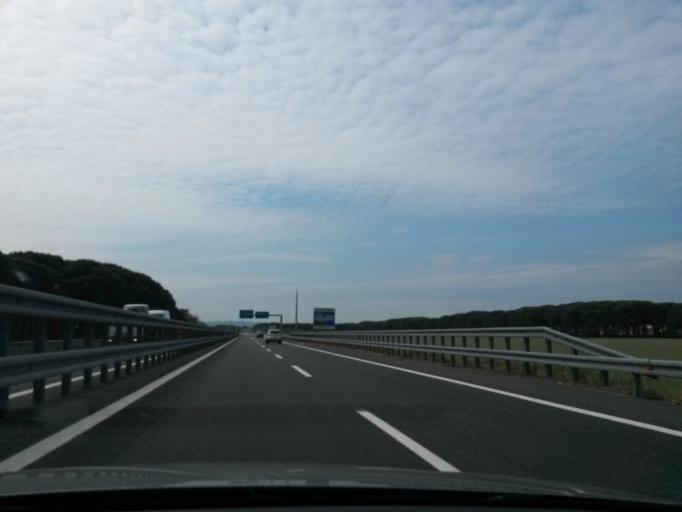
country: IT
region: Tuscany
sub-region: Provincia di Livorno
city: Guasticce
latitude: 43.6221
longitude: 10.3568
